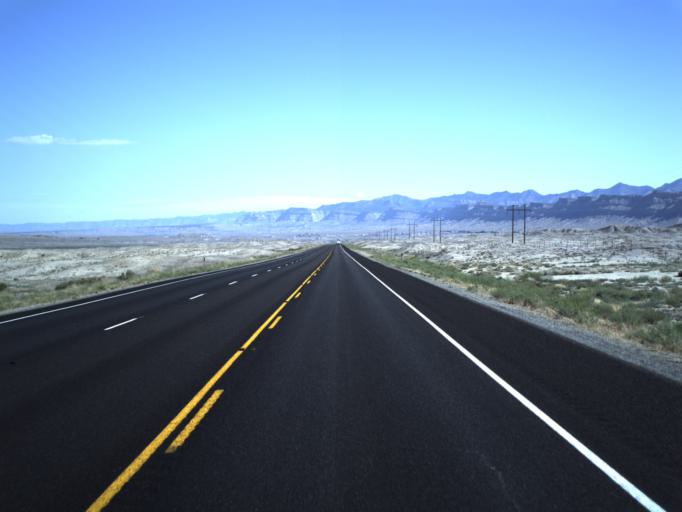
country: US
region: Utah
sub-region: Carbon County
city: East Carbon City
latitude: 39.1986
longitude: -110.3385
